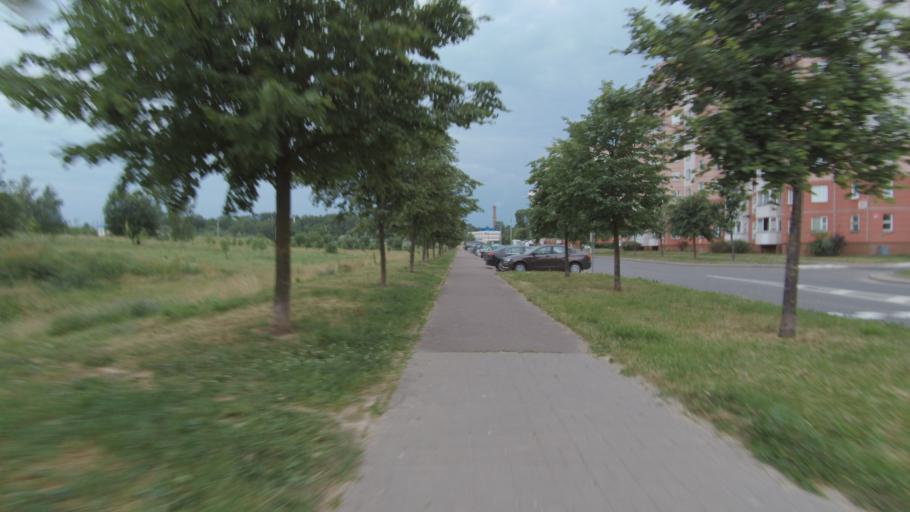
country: BY
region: Minsk
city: Syenitsa
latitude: 53.8408
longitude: 27.5674
